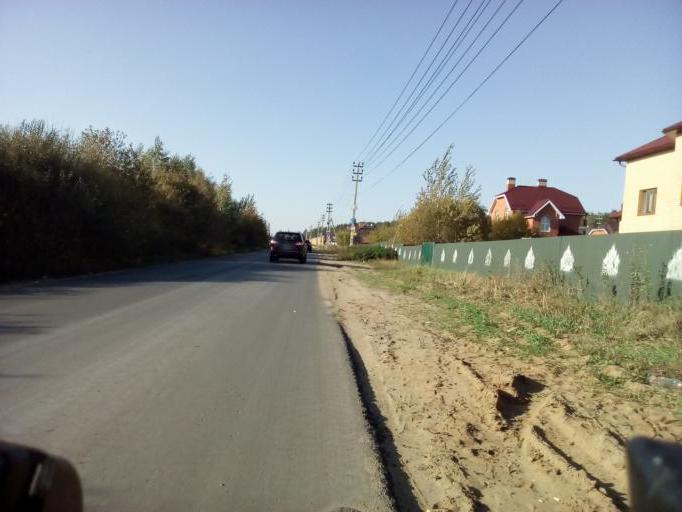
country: RU
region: Moskovskaya
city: Malyshevo
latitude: 55.5583
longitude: 38.3097
